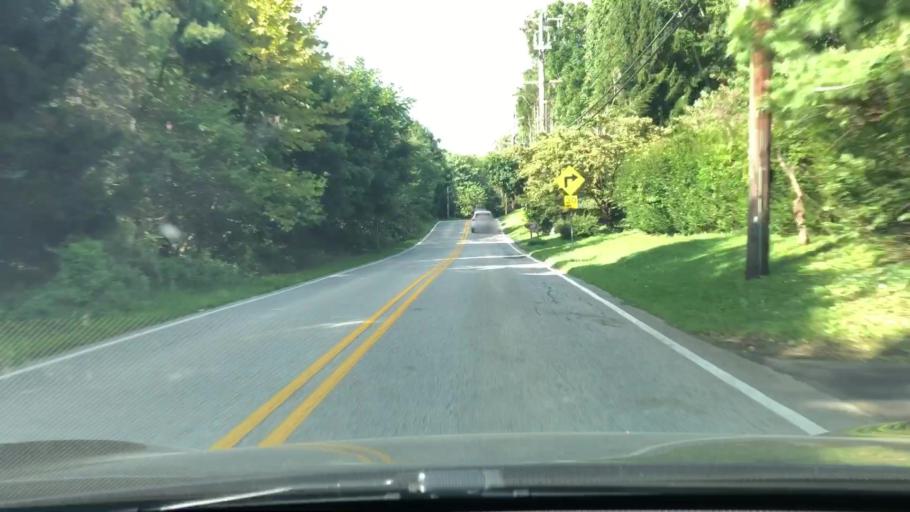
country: US
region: Pennsylvania
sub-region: Delaware County
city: Wayne
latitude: 40.0194
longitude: -75.4044
